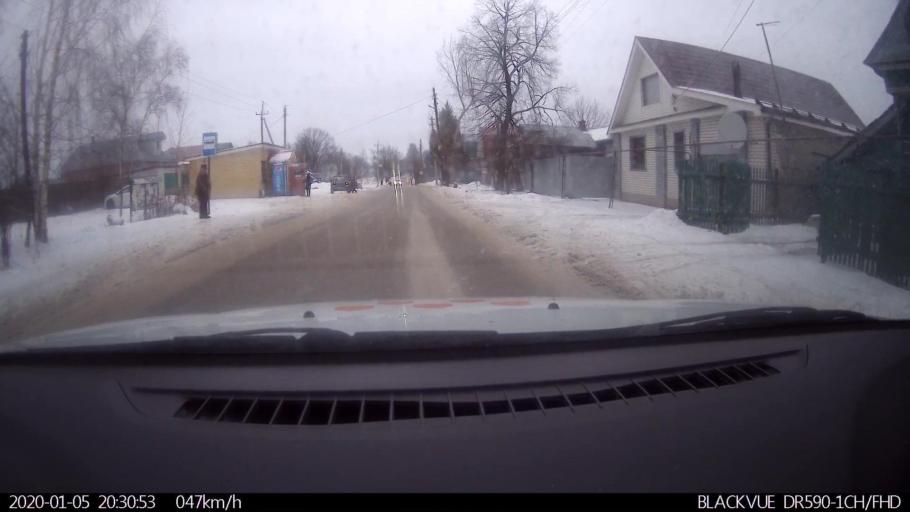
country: RU
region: Nizjnij Novgorod
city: Lukino
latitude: 56.4021
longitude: 43.7293
